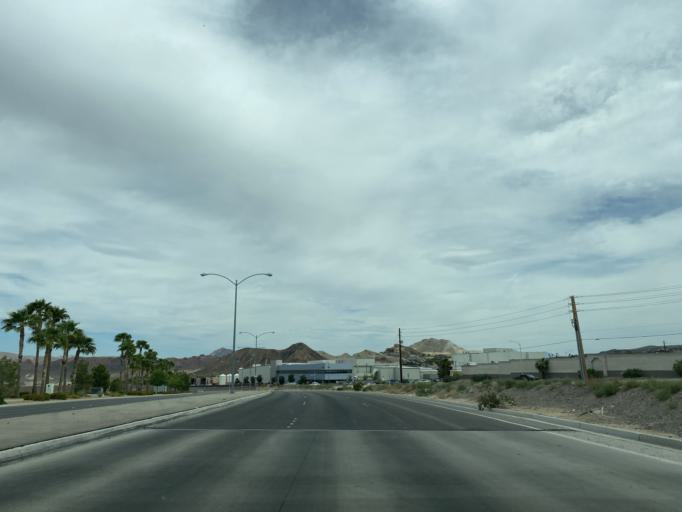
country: US
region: Nevada
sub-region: Clark County
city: Henderson
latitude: 36.0743
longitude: -114.9584
